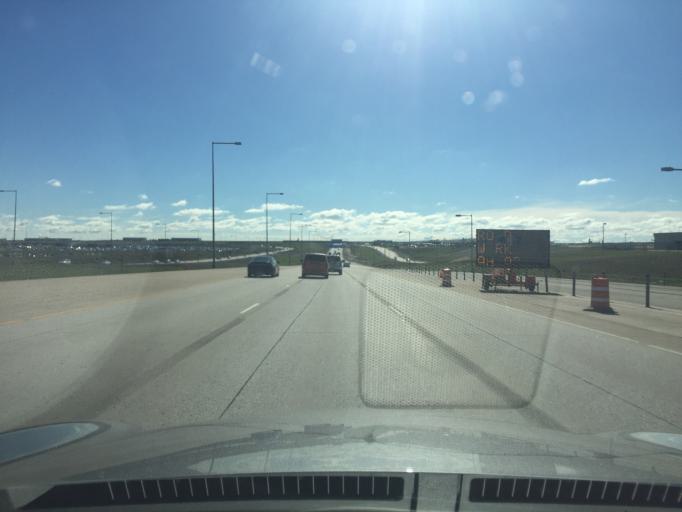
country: US
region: Colorado
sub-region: Weld County
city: Lochbuie
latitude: 39.8335
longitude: -104.6897
